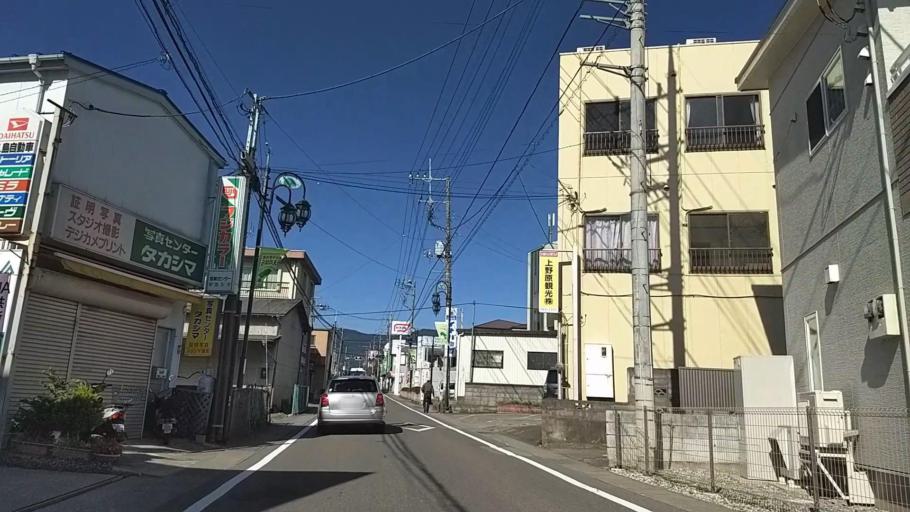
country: JP
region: Yamanashi
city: Uenohara
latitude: 35.6319
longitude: 139.1096
